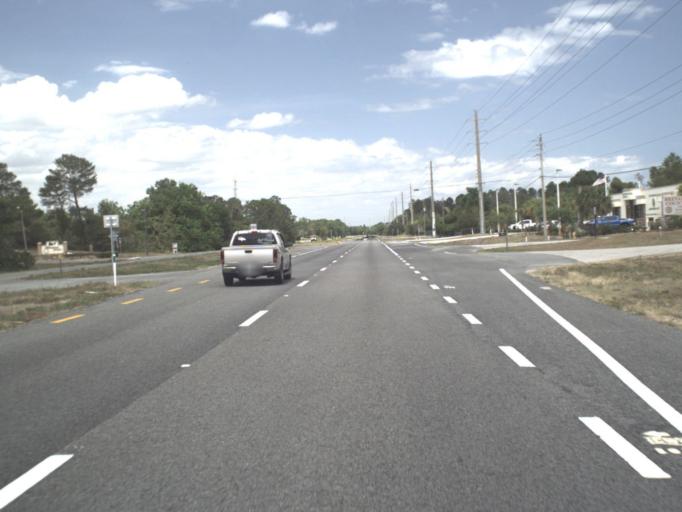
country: US
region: Florida
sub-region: Brevard County
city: Titusville
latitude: 28.5416
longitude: -80.8299
